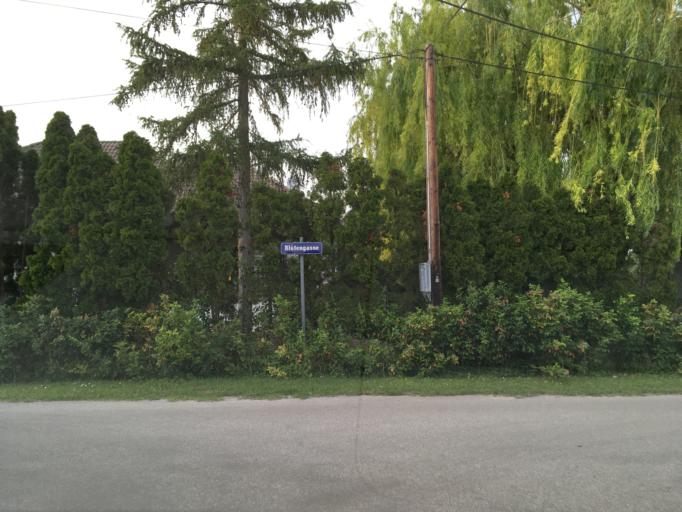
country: AT
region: Lower Austria
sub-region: Politischer Bezirk Wien-Umgebung
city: Gerasdorf bei Wien
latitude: 48.3193
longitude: 16.5000
